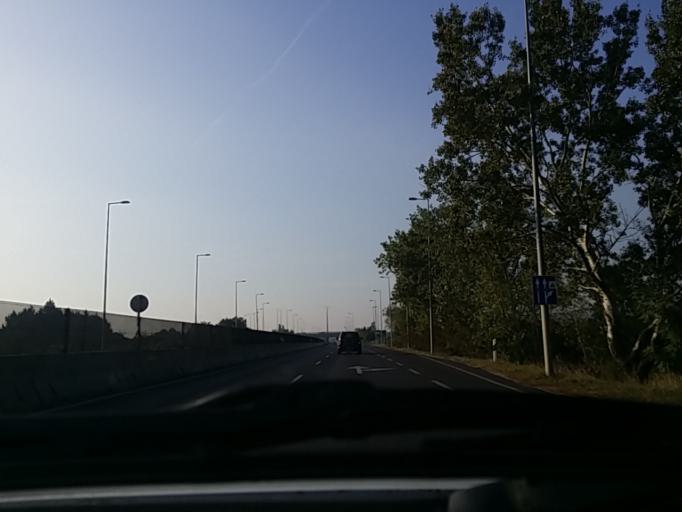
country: HU
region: Pest
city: Budakalasz
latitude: 47.6233
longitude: 19.0674
